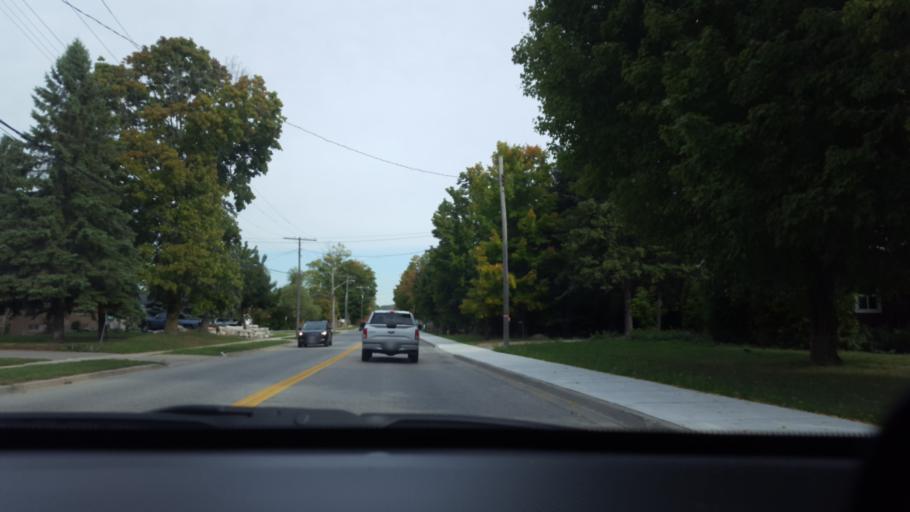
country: CA
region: Ontario
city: Vaughan
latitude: 43.9320
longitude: -79.5291
